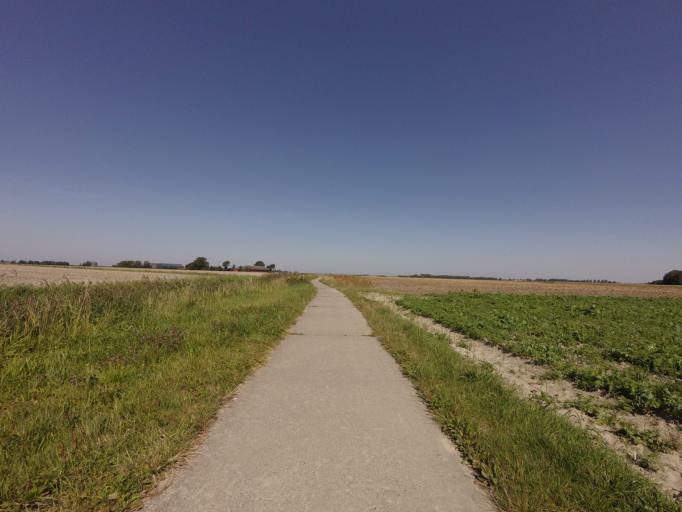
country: NL
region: Friesland
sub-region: Gemeente Dongeradeel
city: Anjum
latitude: 53.3879
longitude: 6.0660
